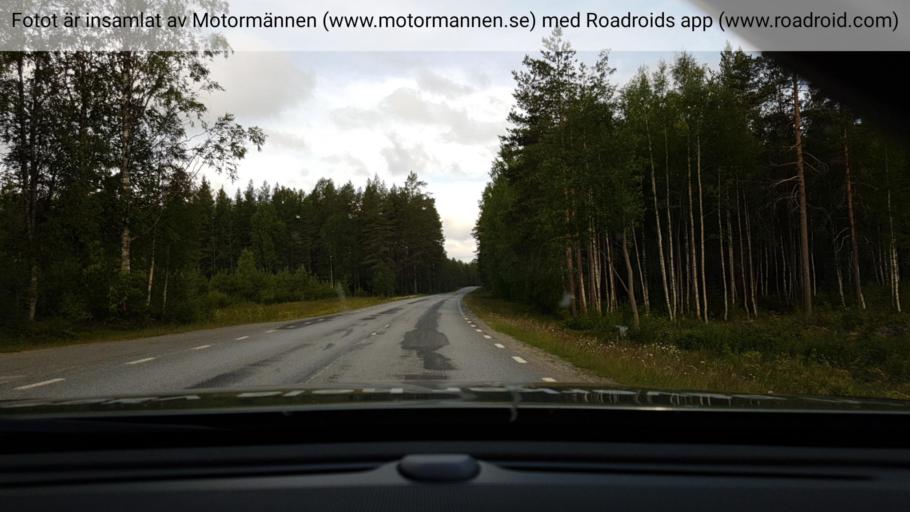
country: SE
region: Vaesterbotten
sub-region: Vindelns Kommun
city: Vindeln
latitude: 64.2438
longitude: 19.6608
